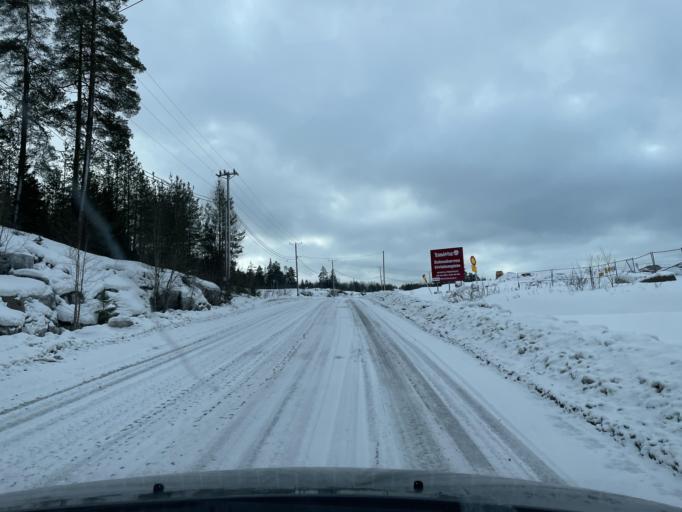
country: FI
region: Uusimaa
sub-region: Helsinki
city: Espoo
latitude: 60.2428
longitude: 24.5603
